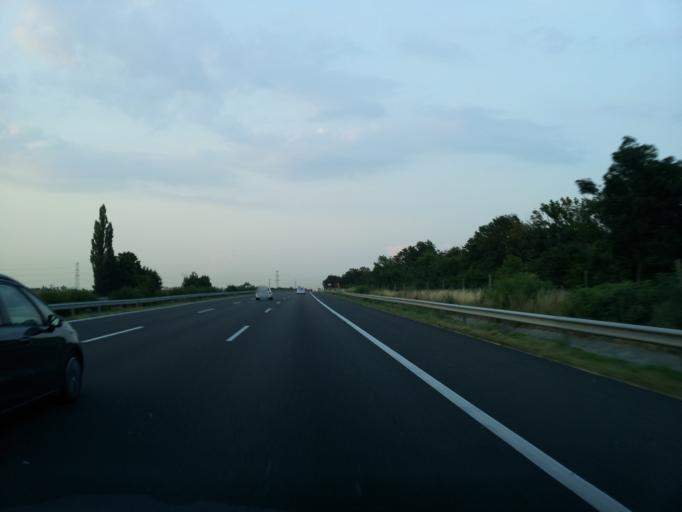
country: HU
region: Fejer
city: Martonvasar
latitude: 47.3448
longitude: 18.7932
